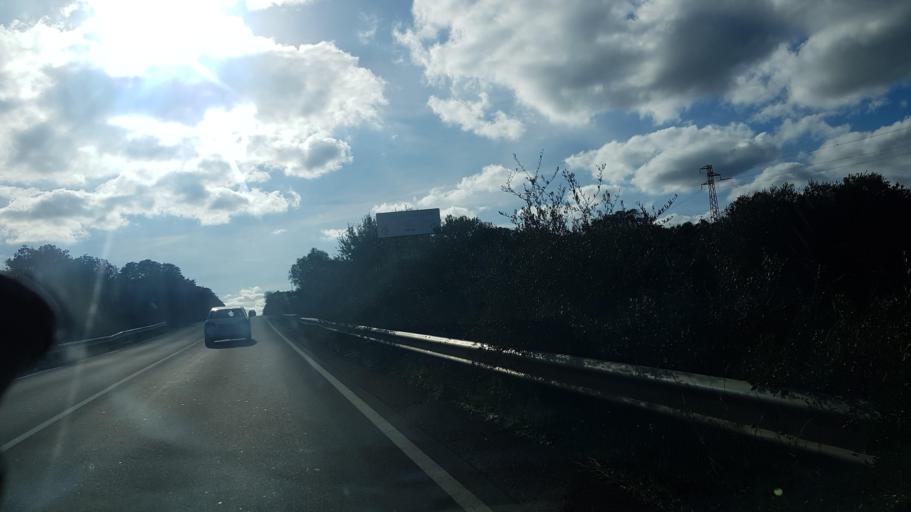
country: IT
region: Apulia
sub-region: Provincia di Brindisi
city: Ceglie Messapica
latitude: 40.6777
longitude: 17.5437
